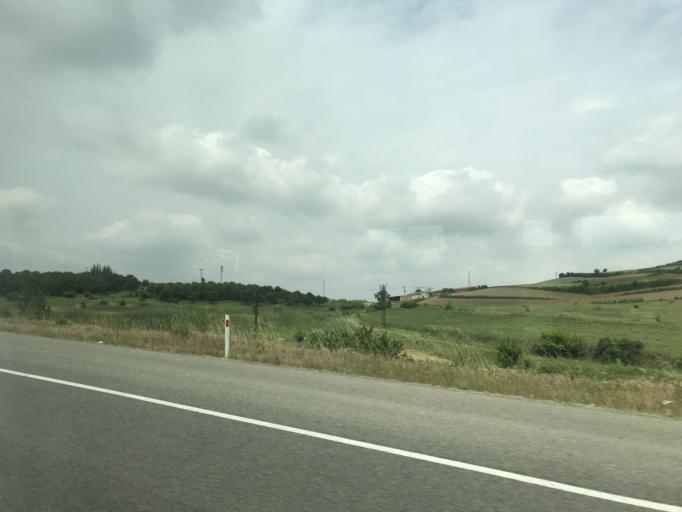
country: TR
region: Tekirdag
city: Inecik
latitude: 40.9392
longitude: 27.2752
